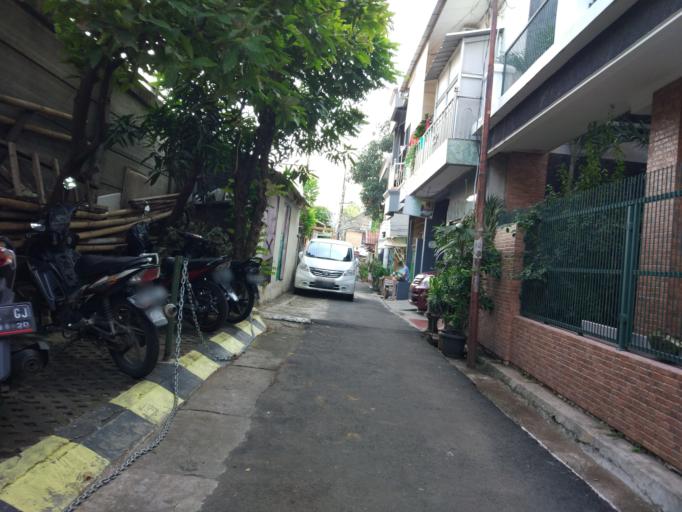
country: ID
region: Jakarta Raya
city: Jakarta
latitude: -6.2409
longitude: 106.8588
